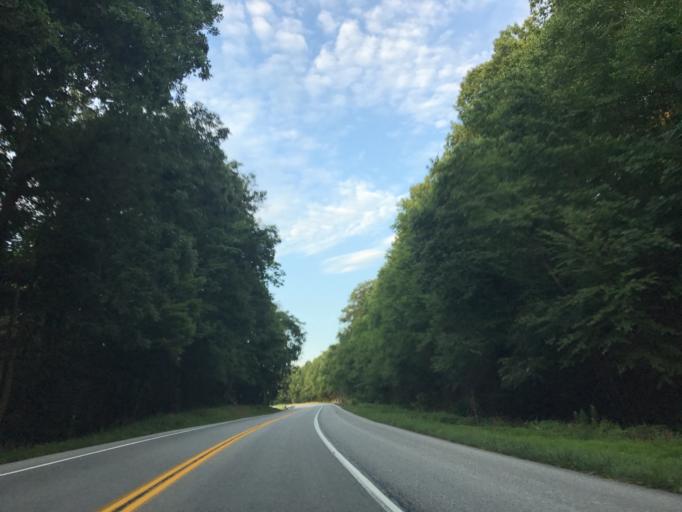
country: US
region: Pennsylvania
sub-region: York County
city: Susquehanna Trails
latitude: 39.8249
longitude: -76.3155
